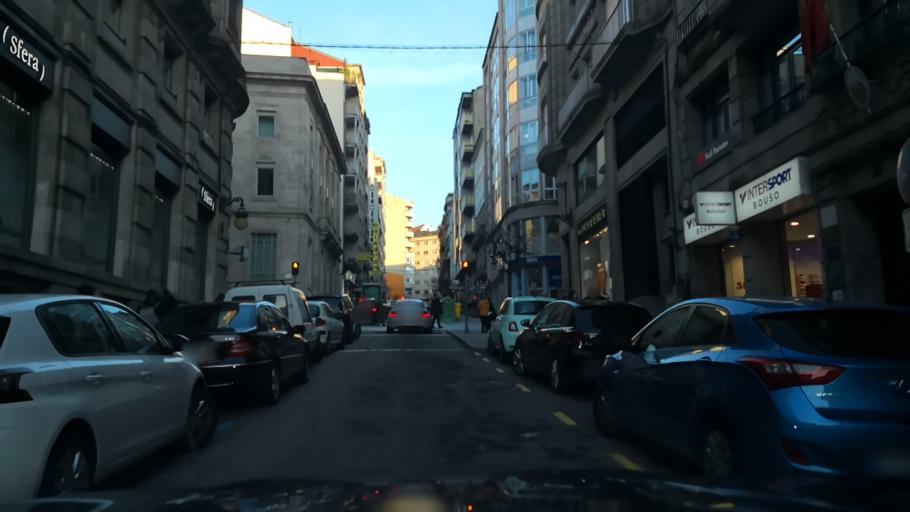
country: ES
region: Galicia
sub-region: Provincia de Ourense
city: Ourense
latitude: 42.3395
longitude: -7.8653
